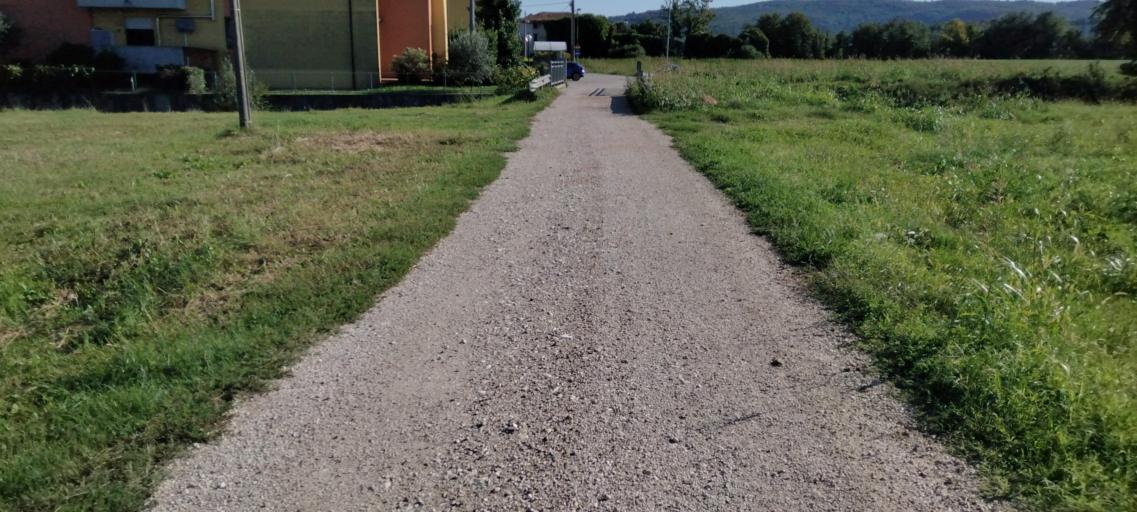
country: IT
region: Veneto
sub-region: Provincia di Vicenza
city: Creazzo
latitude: 45.5253
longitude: 11.4821
